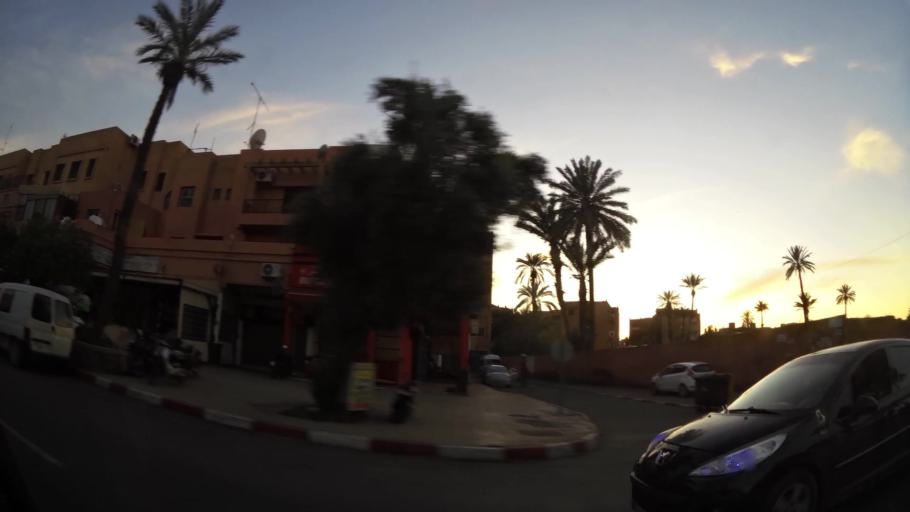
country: MA
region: Marrakech-Tensift-Al Haouz
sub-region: Marrakech
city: Marrakesh
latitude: 31.6420
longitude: -8.0002
